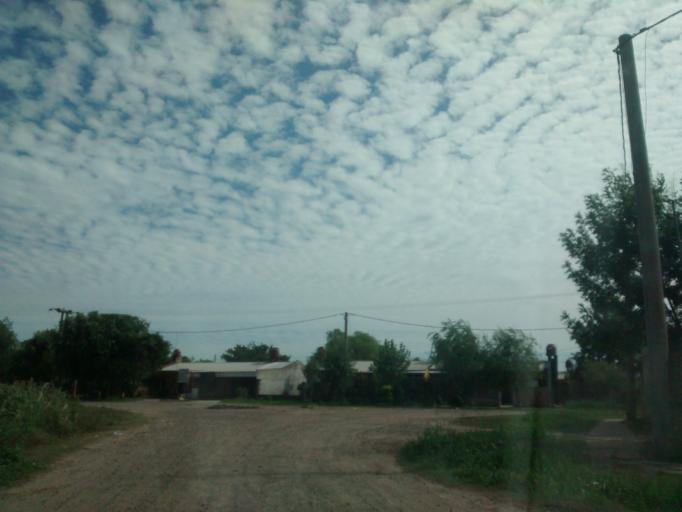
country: AR
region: Chaco
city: Fontana
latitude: -27.3993
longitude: -58.9900
